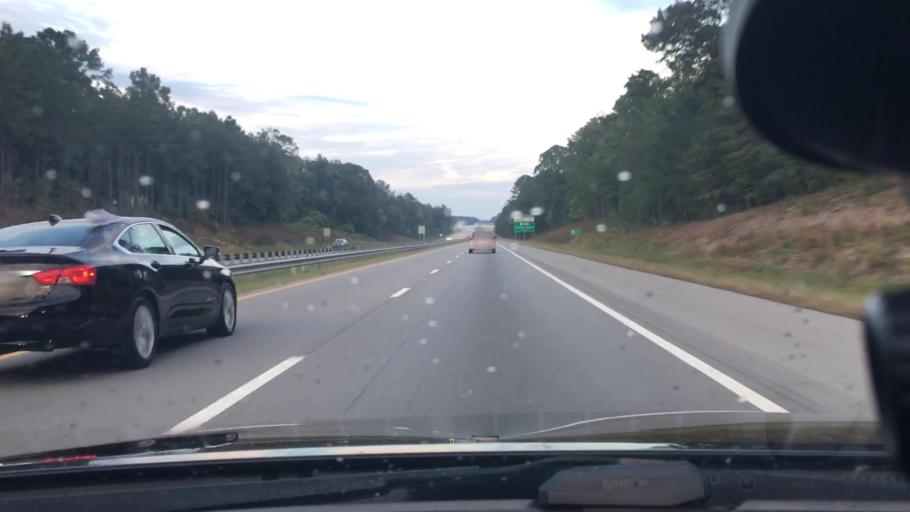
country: US
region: North Carolina
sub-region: Wake County
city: Apex
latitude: 35.6869
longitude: -78.8923
